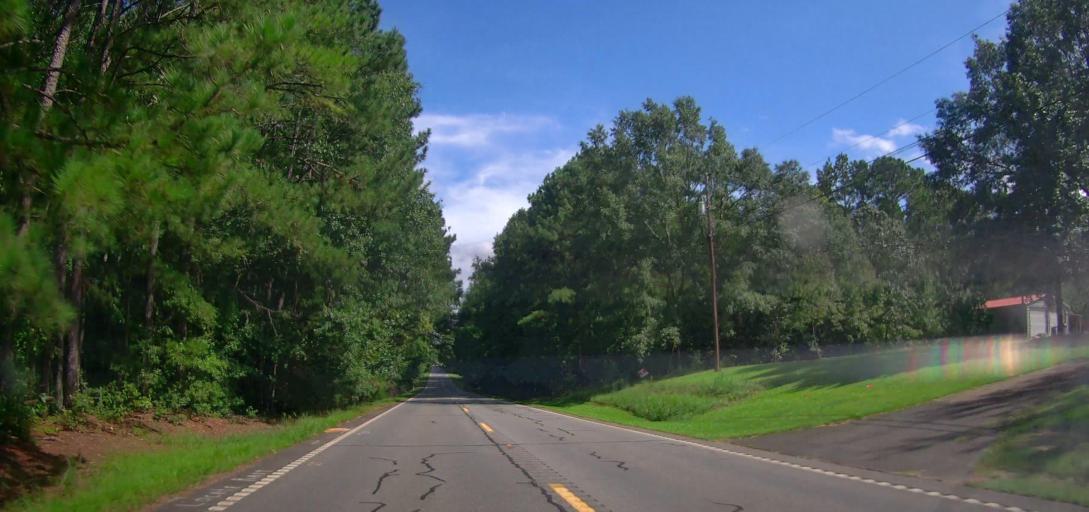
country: US
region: Georgia
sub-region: Talbot County
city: Sardis
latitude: 32.8204
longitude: -84.6090
